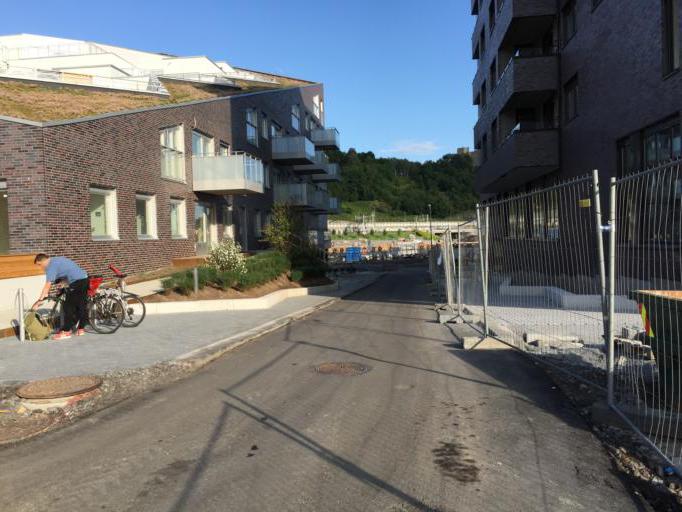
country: NO
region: Oslo
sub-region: Oslo
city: Oslo
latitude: 59.9015
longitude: 10.7524
